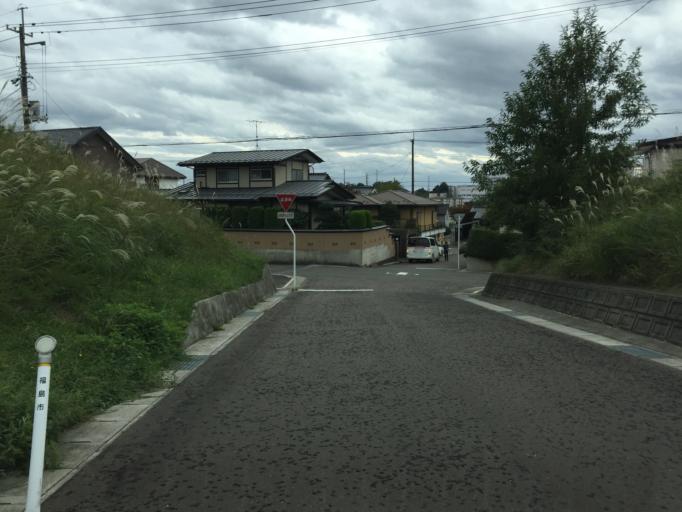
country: JP
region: Fukushima
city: Fukushima-shi
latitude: 37.6961
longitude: 140.4745
